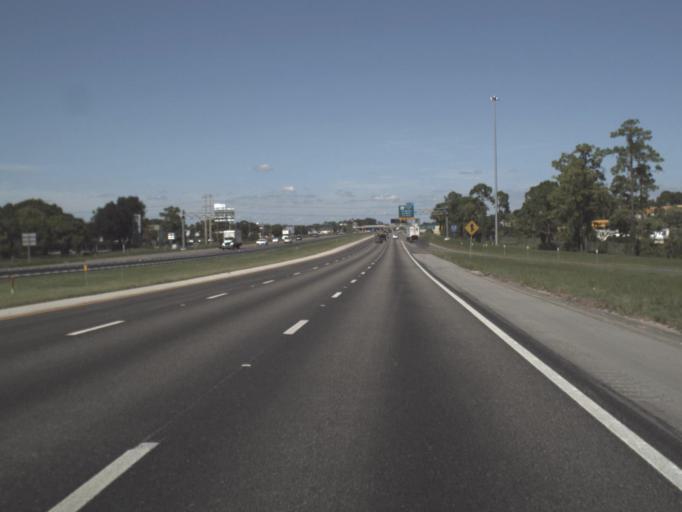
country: US
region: Florida
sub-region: Lee County
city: Tice
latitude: 26.6588
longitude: -81.7994
